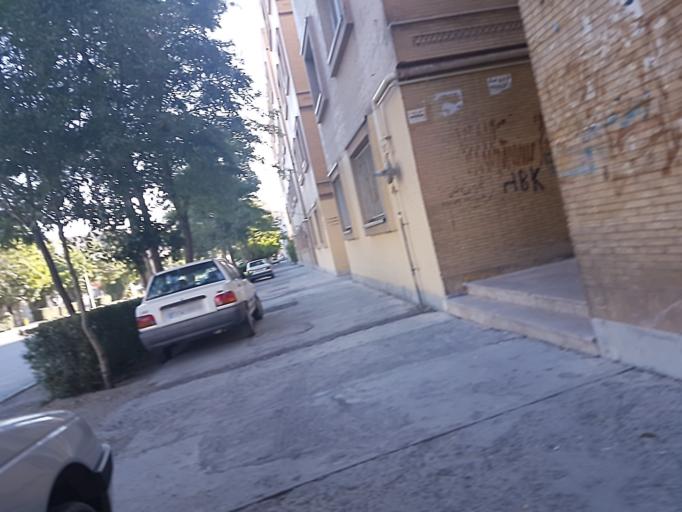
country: IR
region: Markazi
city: Arak
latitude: 34.0649
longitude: 49.6807
